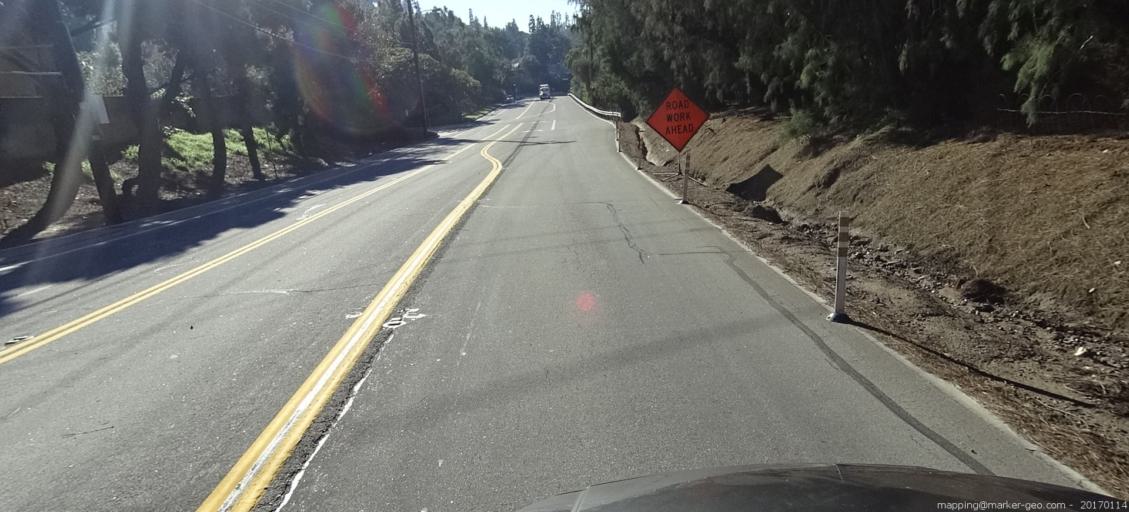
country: US
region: California
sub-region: Orange County
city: North Tustin
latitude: 33.7767
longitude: -117.7881
